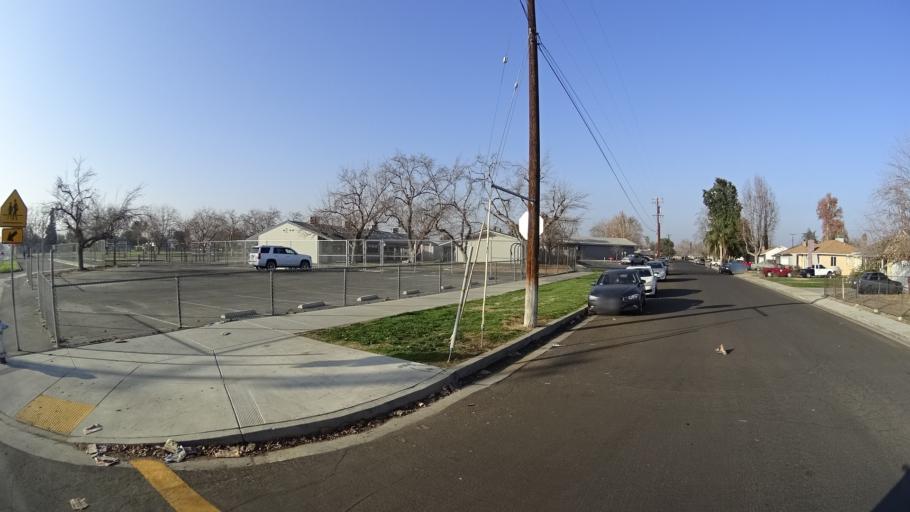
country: US
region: California
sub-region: Kern County
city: Bakersfield
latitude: 35.3485
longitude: -119.0435
